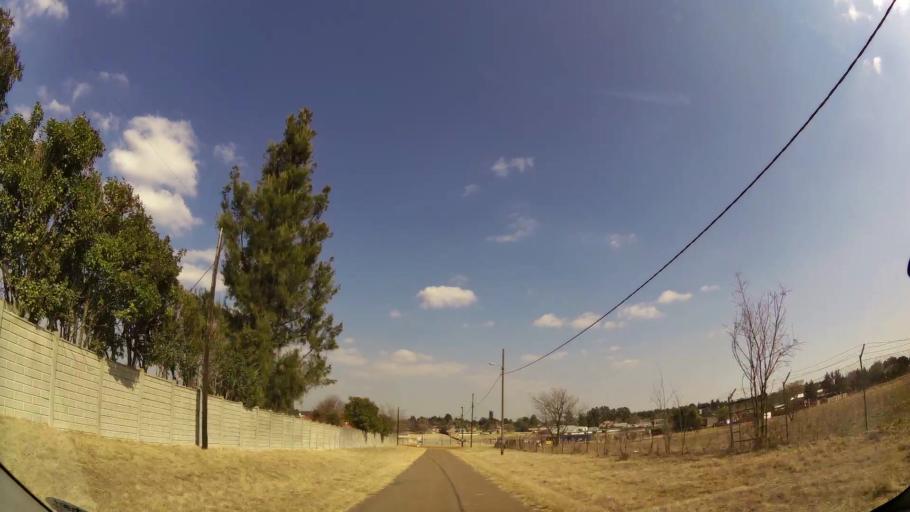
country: ZA
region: Gauteng
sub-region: Ekurhuleni Metropolitan Municipality
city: Benoni
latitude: -26.0784
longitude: 28.3390
